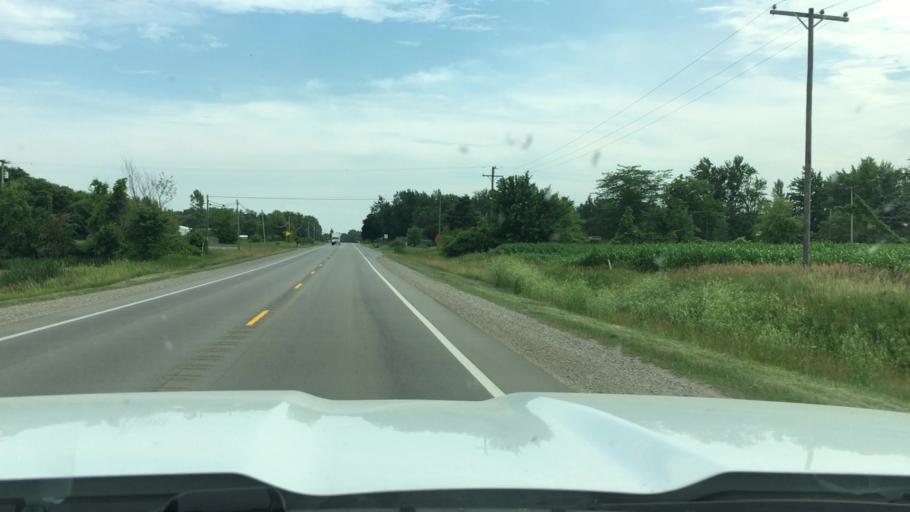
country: US
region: Michigan
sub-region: Sanilac County
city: Marlette
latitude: 43.3504
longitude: -83.0848
